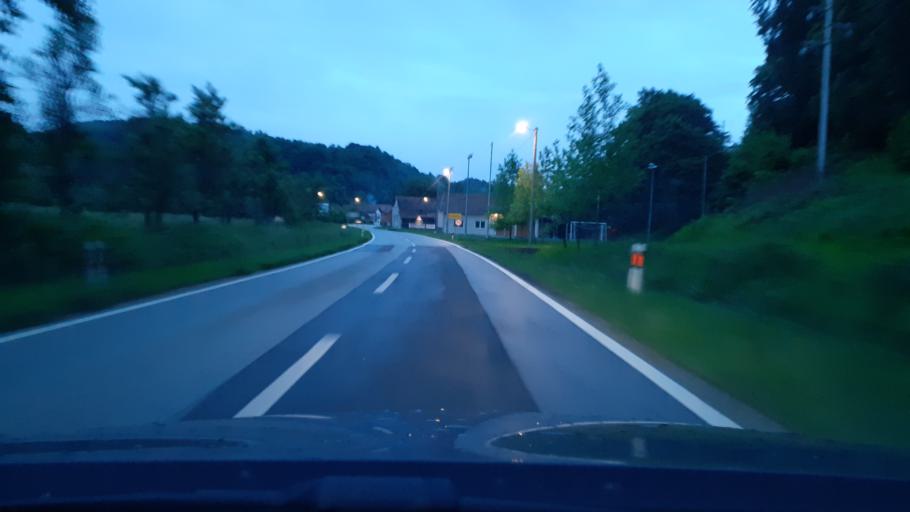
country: HR
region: Pozesko-Slavonska
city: Bilice
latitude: 45.2034
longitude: 17.8441
